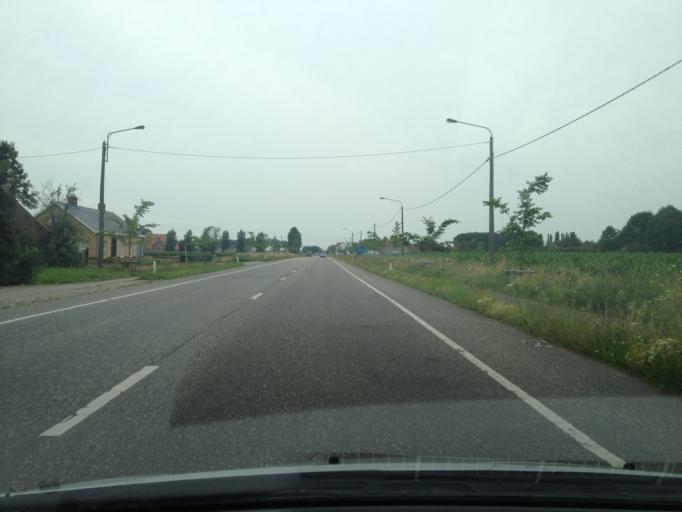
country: BE
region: Flanders
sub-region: Provincie West-Vlaanderen
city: Diksmuide
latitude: 51.0694
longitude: 2.8756
